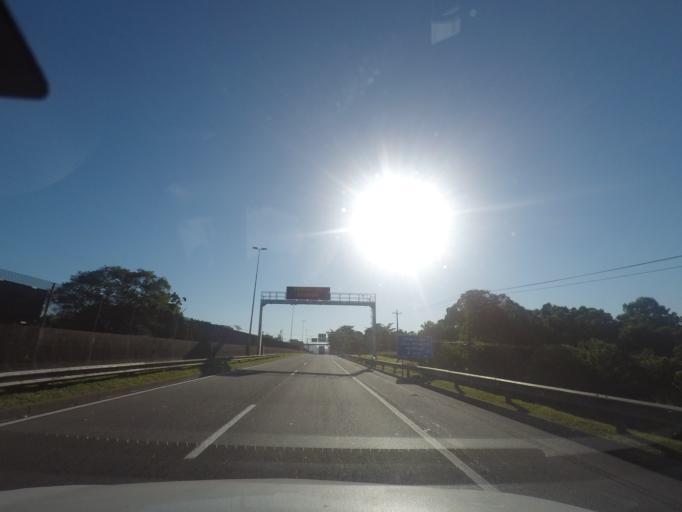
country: BR
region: Rio de Janeiro
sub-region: Petropolis
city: Petropolis
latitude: -22.6467
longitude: -43.1971
